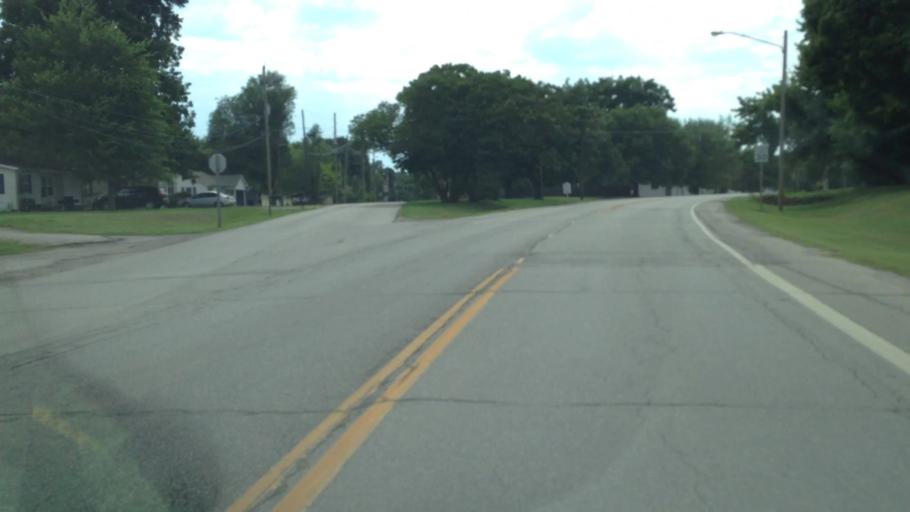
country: US
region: Kansas
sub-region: Labette County
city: Oswego
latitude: 37.1650
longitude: -95.1154
